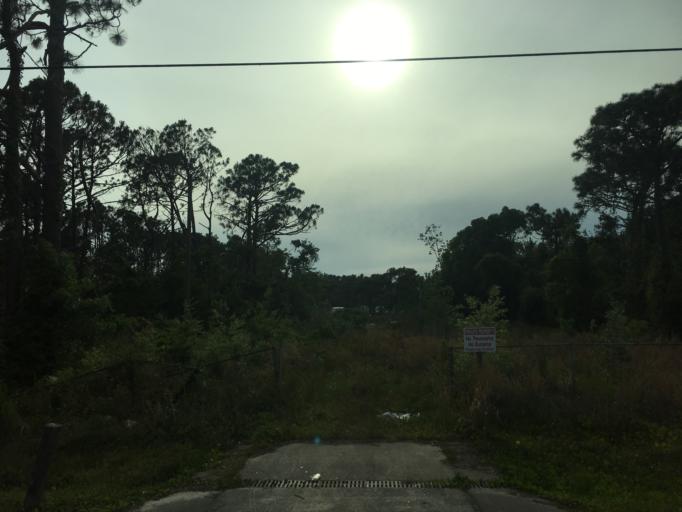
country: US
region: Florida
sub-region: Bay County
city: Panama City Beach
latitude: 30.1734
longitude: -85.7824
